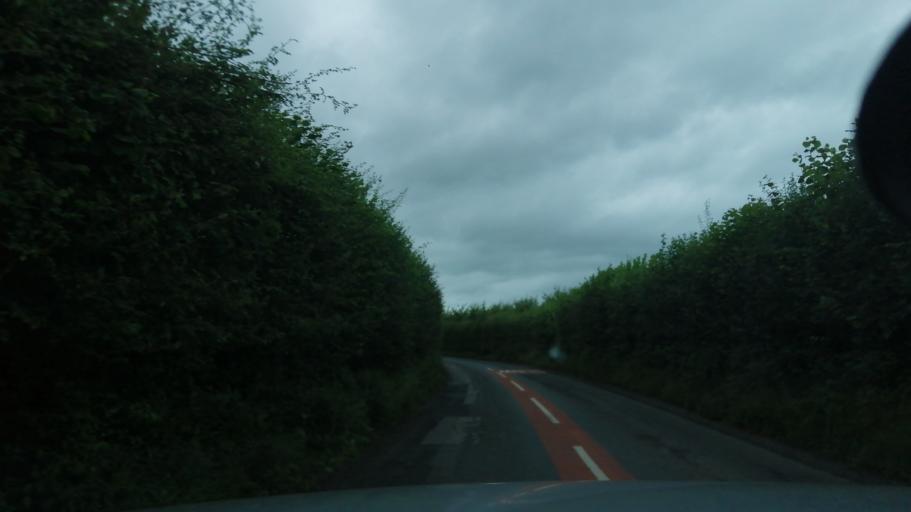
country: GB
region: England
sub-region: Herefordshire
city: Kingstone
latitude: 52.0201
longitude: -2.8560
